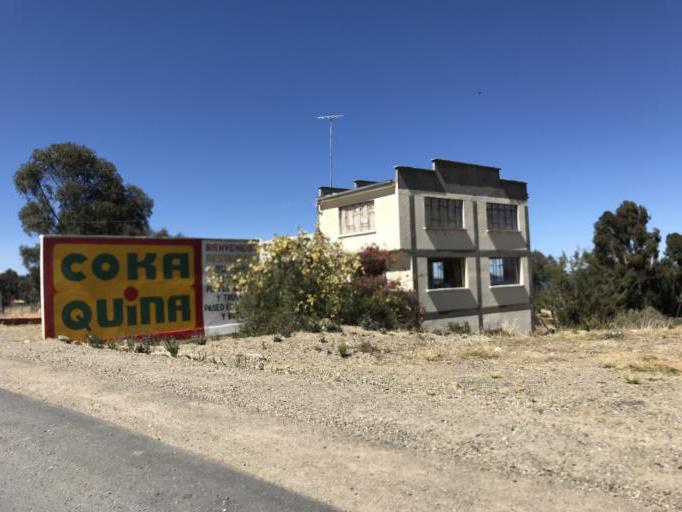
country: BO
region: La Paz
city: Huatajata
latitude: -16.2154
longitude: -68.6629
